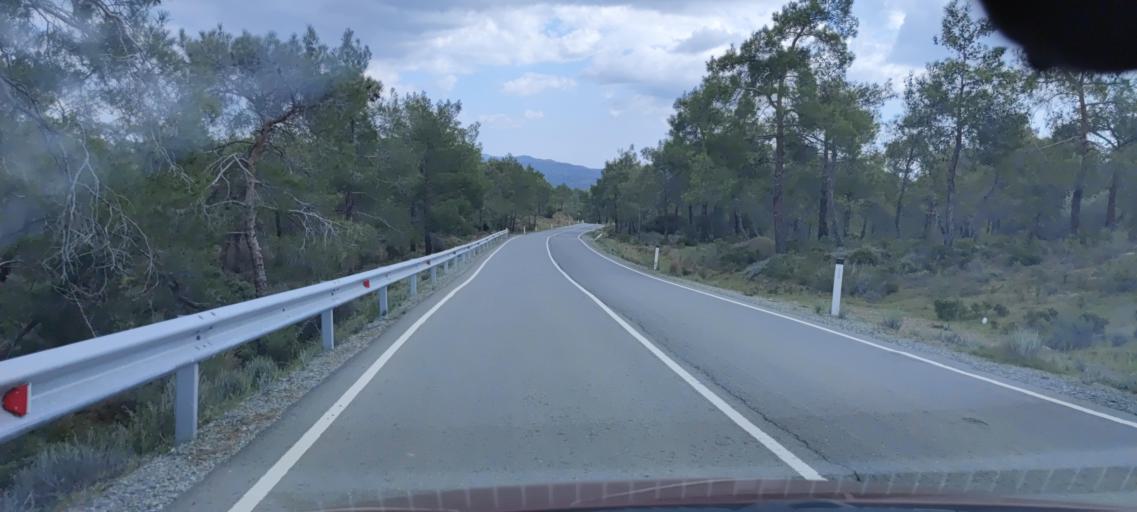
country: CY
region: Lefkosia
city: Lythrodontas
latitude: 34.9316
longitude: 33.3341
